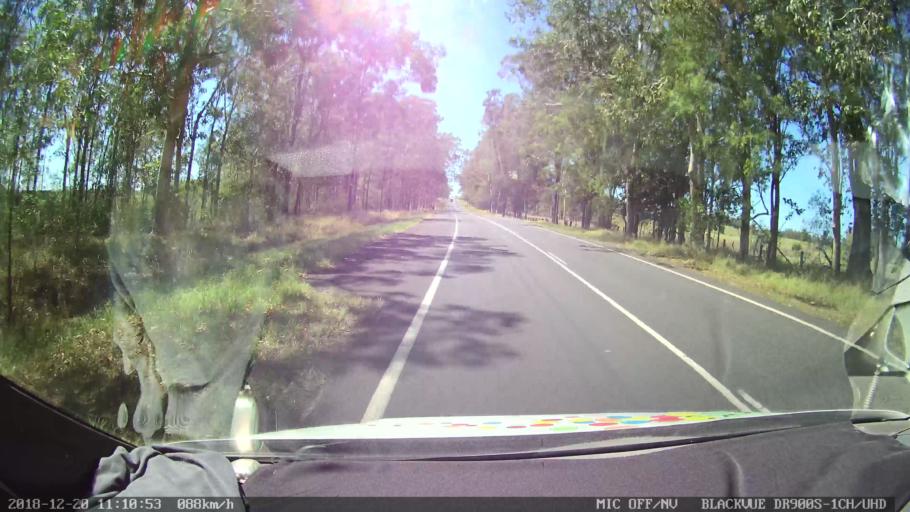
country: AU
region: New South Wales
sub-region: Richmond Valley
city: Casino
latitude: -28.9550
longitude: 153.0111
